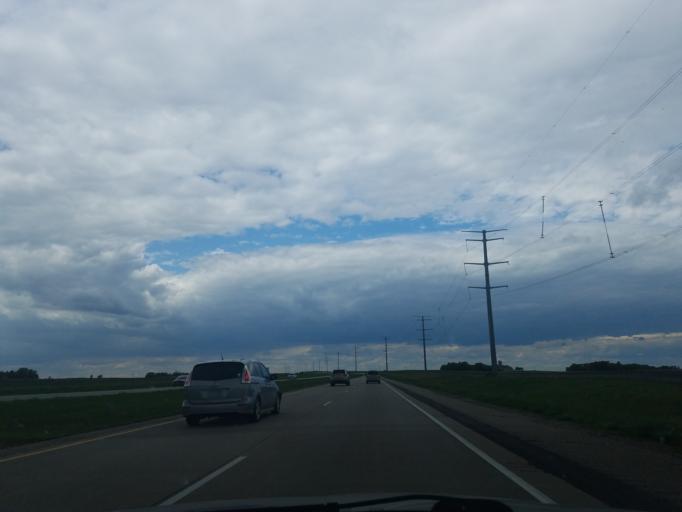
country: US
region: Minnesota
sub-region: Douglas County
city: Osakis
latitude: 45.8048
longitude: -95.1054
